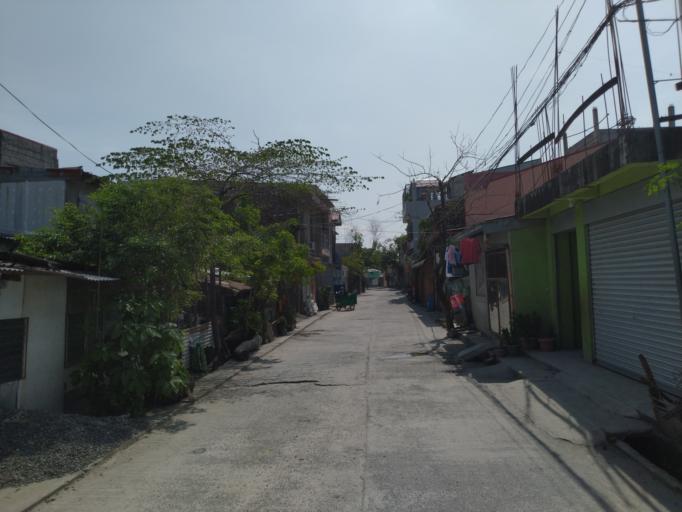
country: PH
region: Calabarzon
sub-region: Province of Rizal
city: Taytay
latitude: 14.5365
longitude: 121.1111
